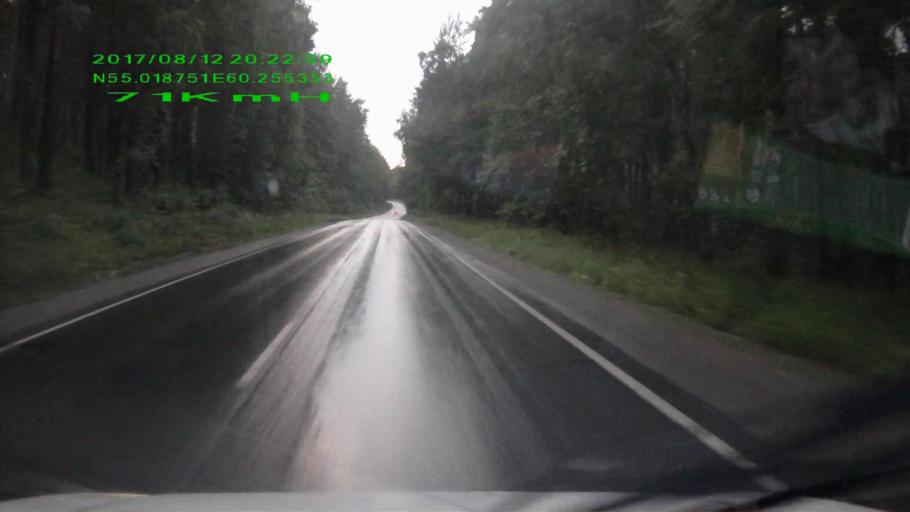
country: RU
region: Chelyabinsk
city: Chebarkul'
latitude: 55.0191
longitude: 60.2550
